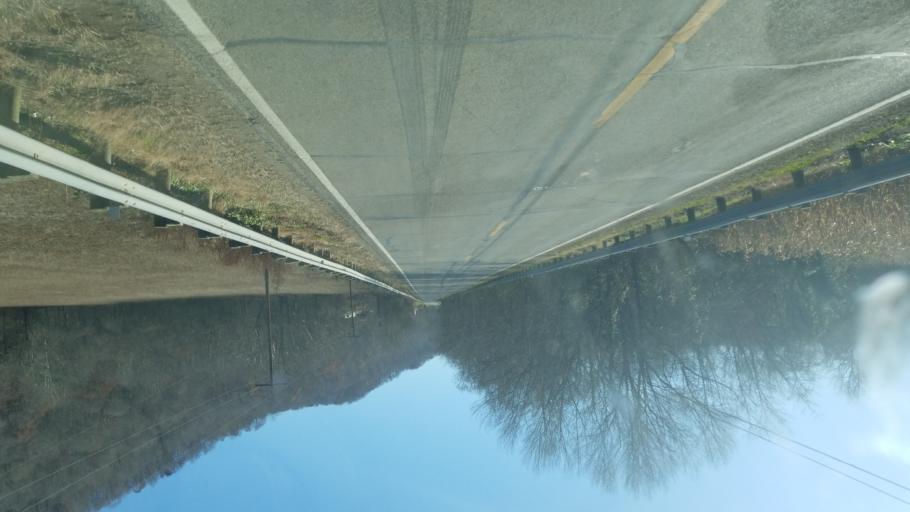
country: US
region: Kentucky
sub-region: Lewis County
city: Vanceburg
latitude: 38.6312
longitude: -83.2548
